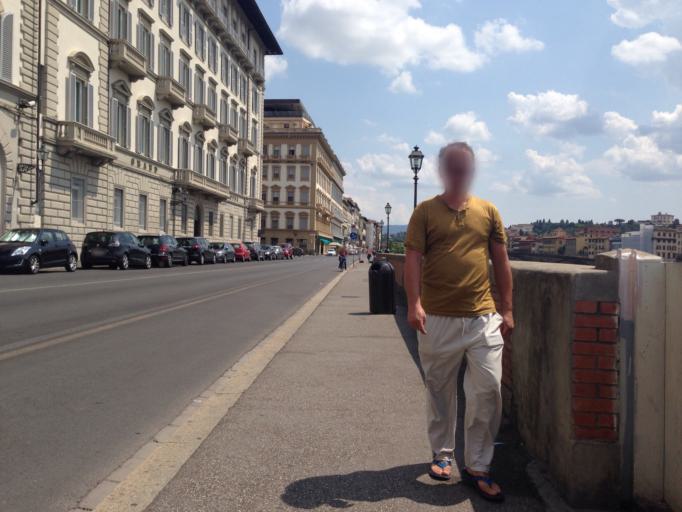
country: IT
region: Tuscany
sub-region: Province of Florence
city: Florence
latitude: 43.7724
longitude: 11.2442
